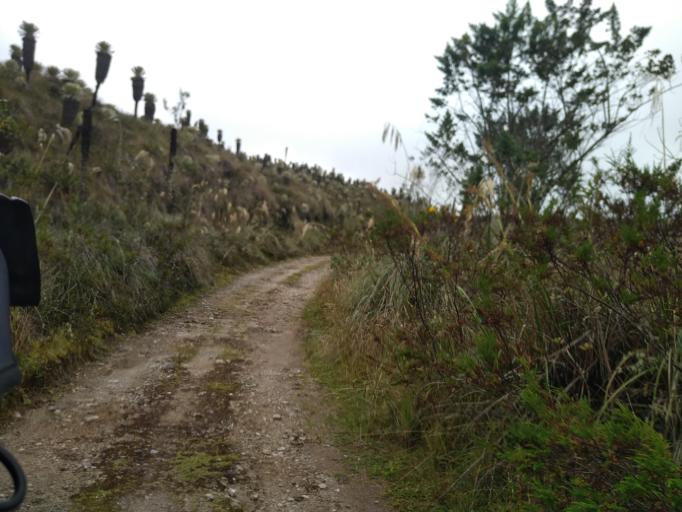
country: EC
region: Carchi
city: San Gabriel
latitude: 0.6918
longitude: -77.8493
